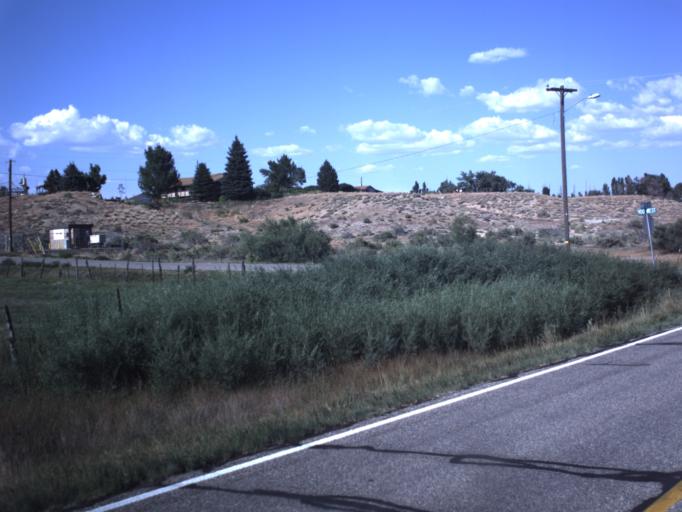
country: US
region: Utah
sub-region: Emery County
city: Huntington
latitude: 39.3475
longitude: -110.8711
